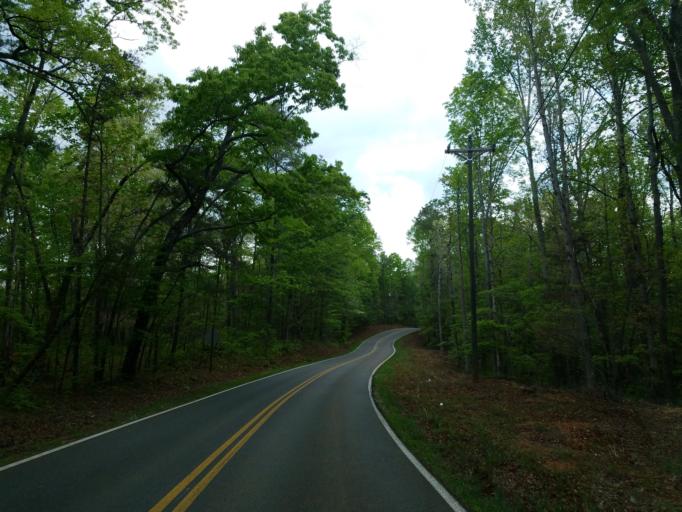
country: US
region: Georgia
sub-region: Pickens County
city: Jasper
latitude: 34.4336
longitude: -84.4600
